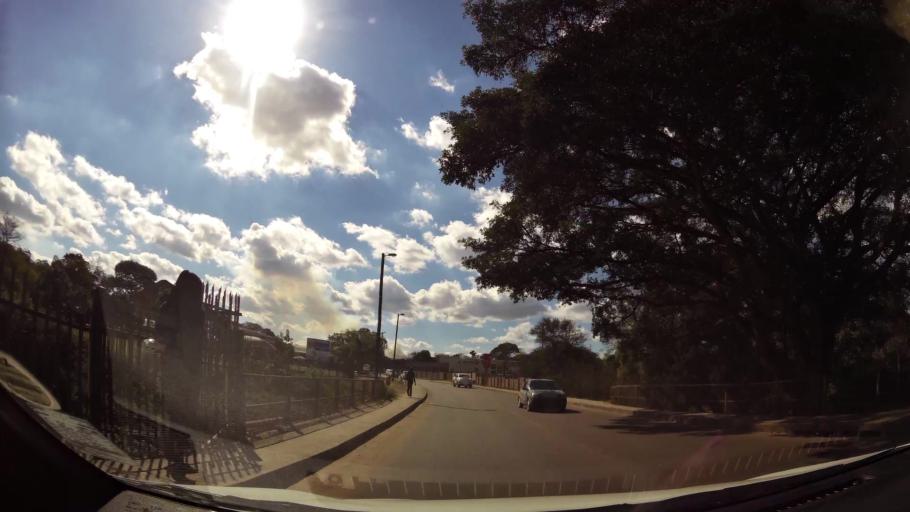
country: ZA
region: Limpopo
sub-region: Mopani District Municipality
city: Tzaneen
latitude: -23.8229
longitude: 30.1630
